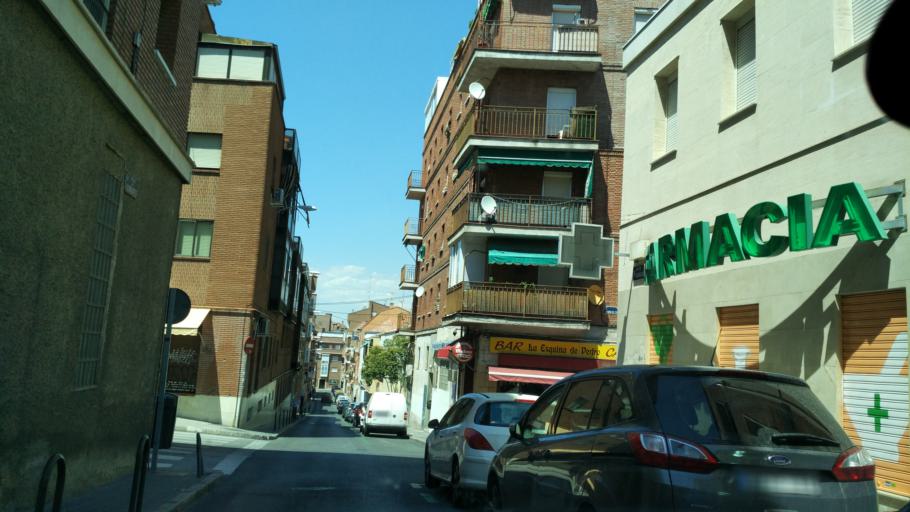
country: ES
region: Madrid
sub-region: Provincia de Madrid
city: Tetuan de las Victorias
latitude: 40.4586
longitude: -3.7048
